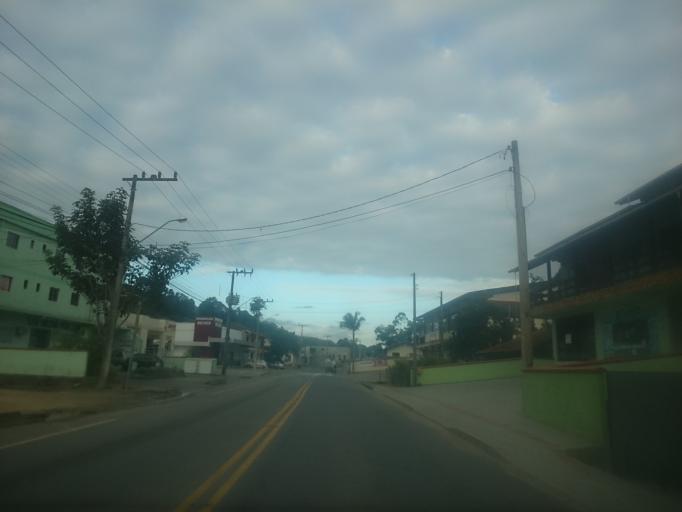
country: BR
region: Santa Catarina
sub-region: Blumenau
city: Blumenau
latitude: -26.8604
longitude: -49.0962
